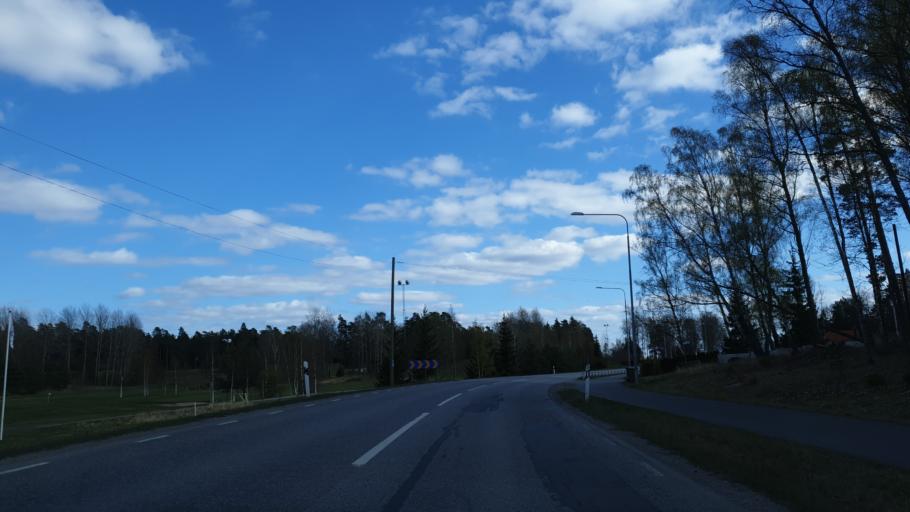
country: SE
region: Stockholm
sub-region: Sigtuna Kommun
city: Rosersberg
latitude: 59.6064
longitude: 17.8804
